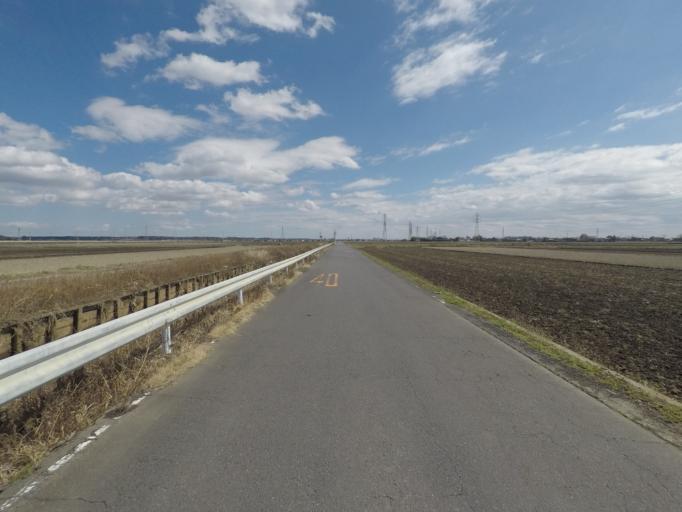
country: JP
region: Ibaraki
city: Fujishiro
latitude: 35.9420
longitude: 140.1038
